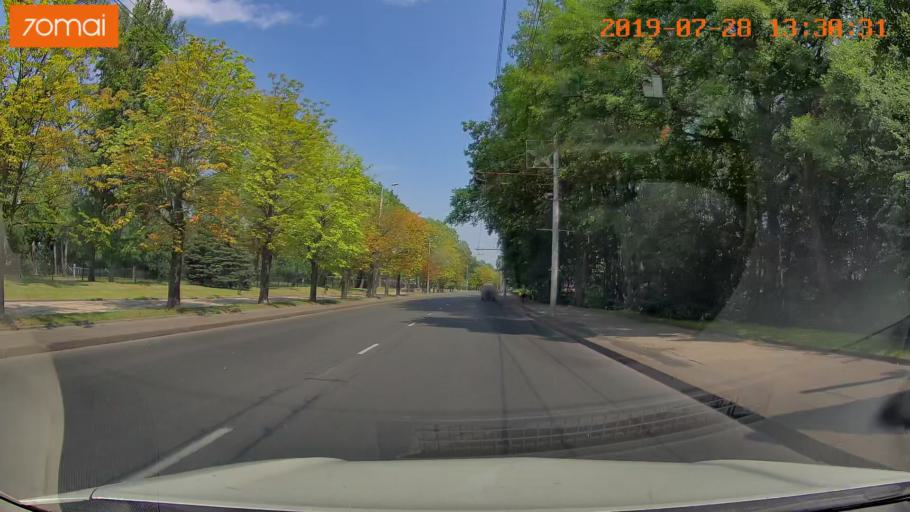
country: RU
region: Kaliningrad
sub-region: Gorod Kaliningrad
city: Kaliningrad
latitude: 54.7152
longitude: 20.4933
